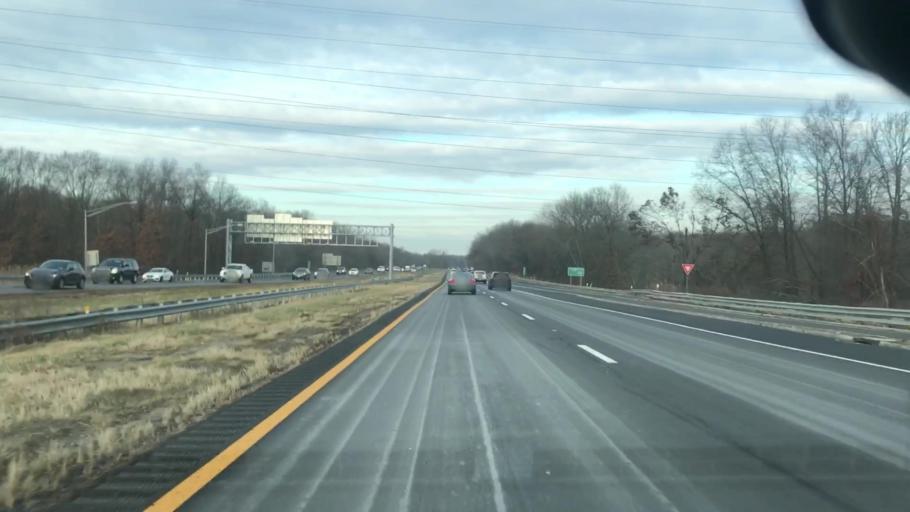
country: US
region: New Jersey
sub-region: Essex County
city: West Caldwell
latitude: 40.8268
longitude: -74.3234
